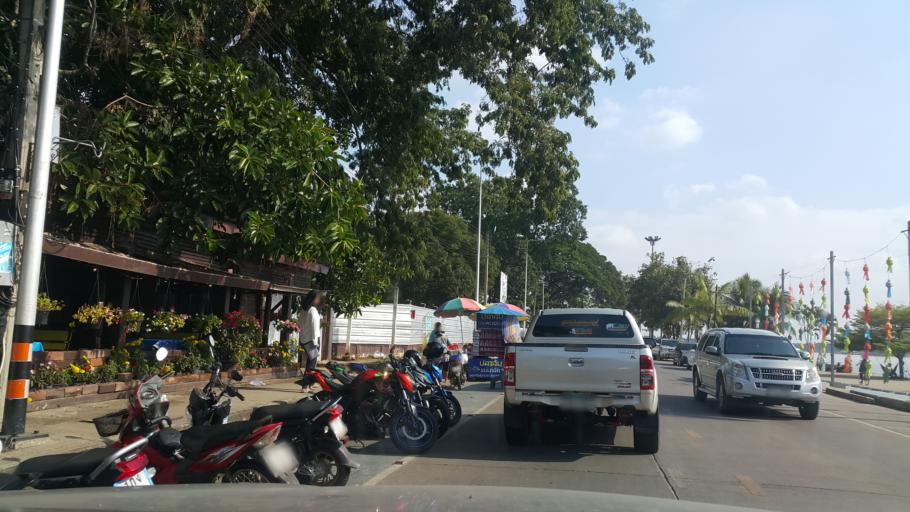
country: TH
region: Phayao
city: Phayao
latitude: 19.1648
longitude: 99.8965
